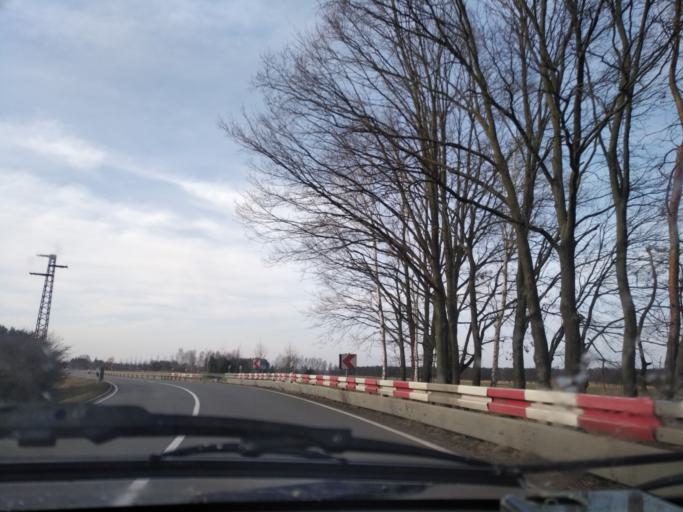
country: DE
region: Brandenburg
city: Schilda
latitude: 51.5971
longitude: 13.3549
